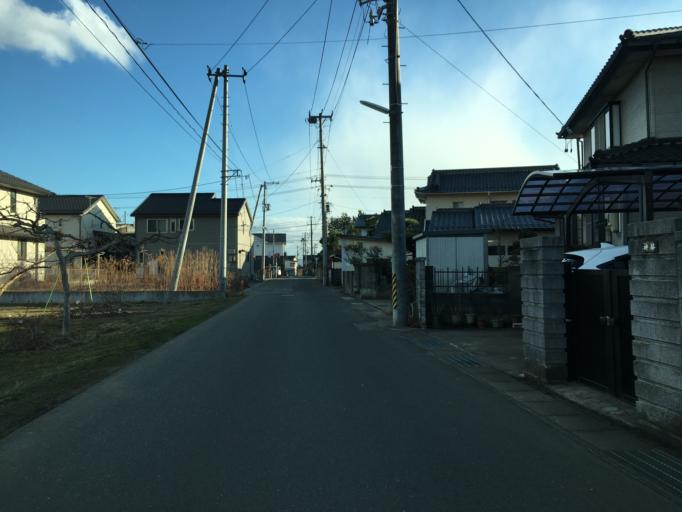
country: JP
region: Fukushima
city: Fukushima-shi
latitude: 37.7778
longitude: 140.4314
